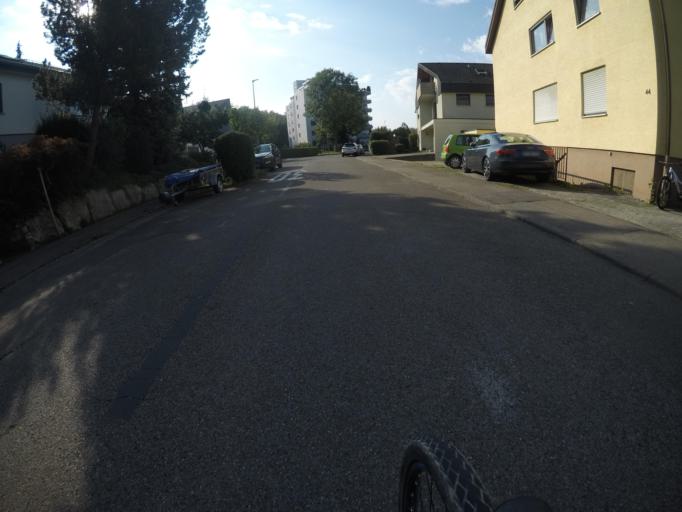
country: DE
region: Baden-Wuerttemberg
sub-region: Tuebingen Region
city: Riederich
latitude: 48.5569
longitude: 9.2732
